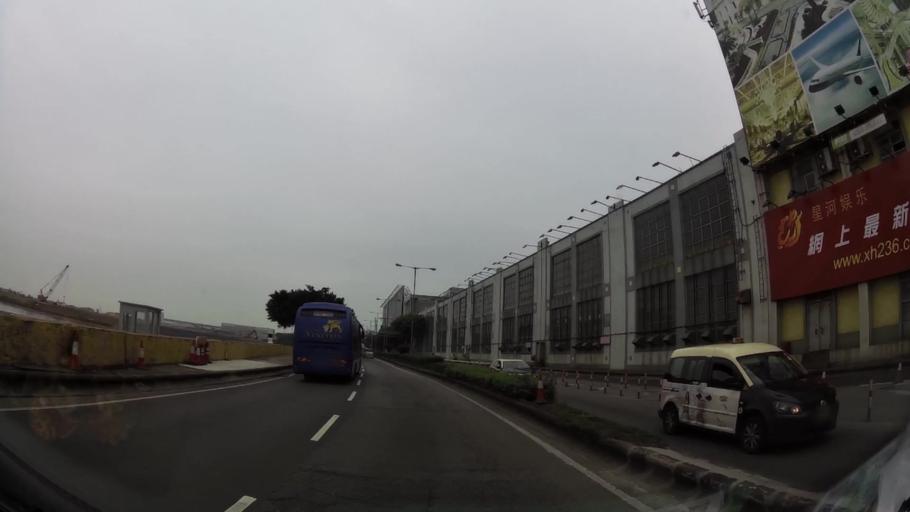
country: MO
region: Macau
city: Macau
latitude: 22.1649
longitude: 113.5646
